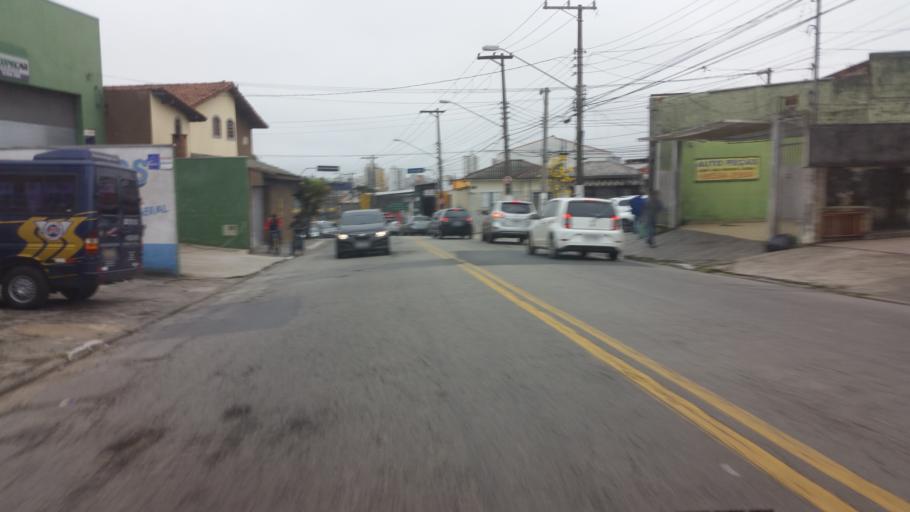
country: BR
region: Sao Paulo
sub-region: Diadema
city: Diadema
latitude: -23.6360
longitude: -46.6146
